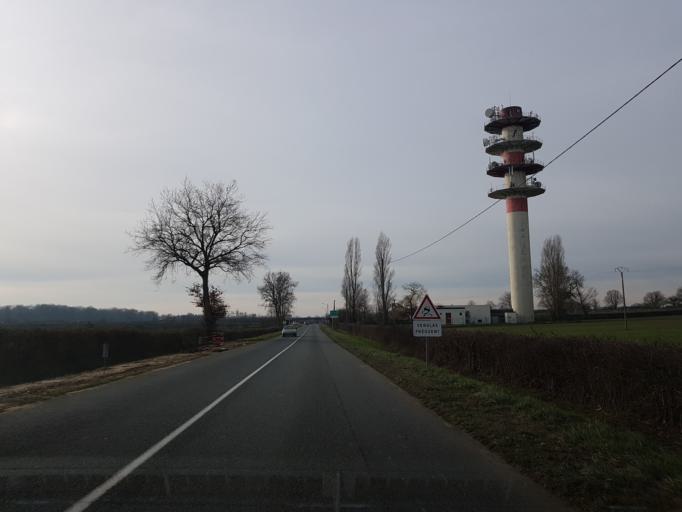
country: FR
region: Auvergne
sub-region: Departement de l'Allier
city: Yzeure
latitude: 46.5796
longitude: 3.3843
